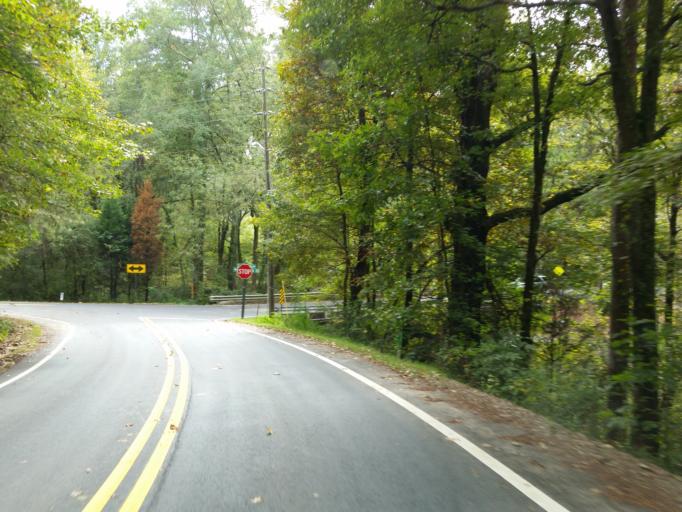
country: US
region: Georgia
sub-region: Fulton County
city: Roswell
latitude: 34.0028
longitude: -84.4458
